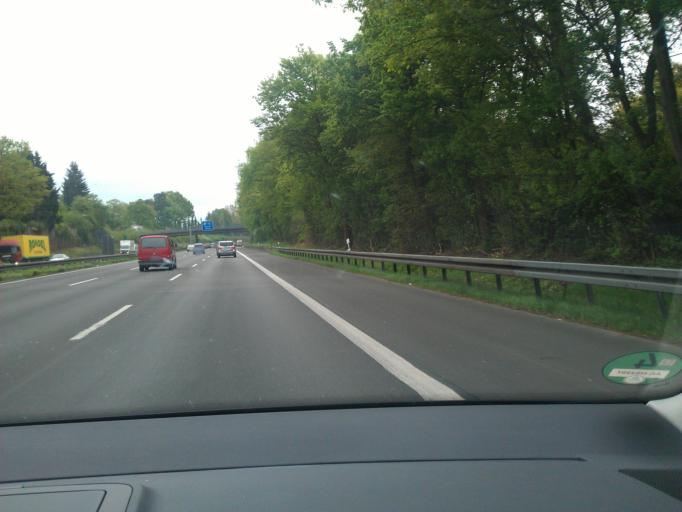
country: DE
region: North Rhine-Westphalia
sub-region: Regierungsbezirk Koln
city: Rosrath
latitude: 50.8962
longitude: 7.1609
